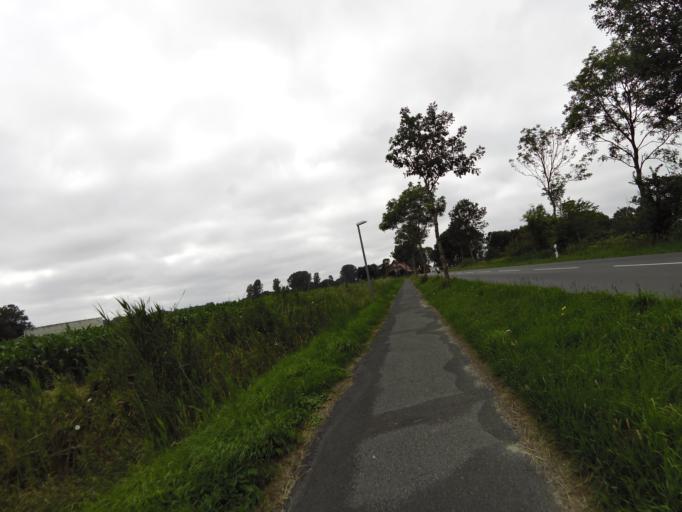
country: DE
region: Lower Saxony
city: Padingbuttel
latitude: 53.7231
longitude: 8.5407
